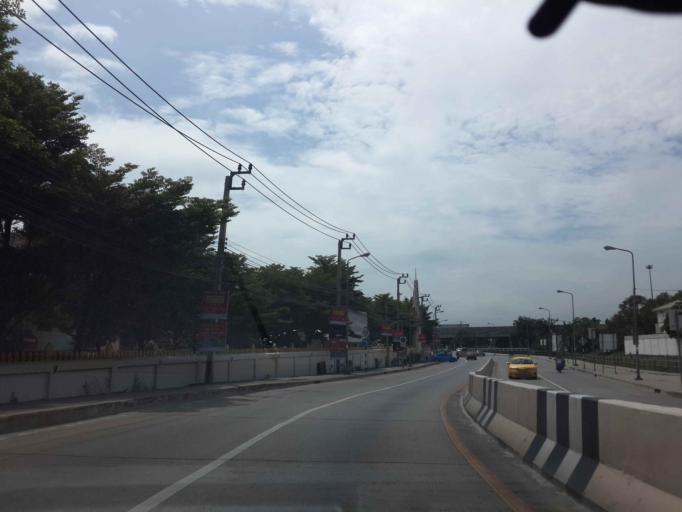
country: TH
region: Bangkok
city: Khan Na Yao
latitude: 13.8526
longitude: 100.6712
